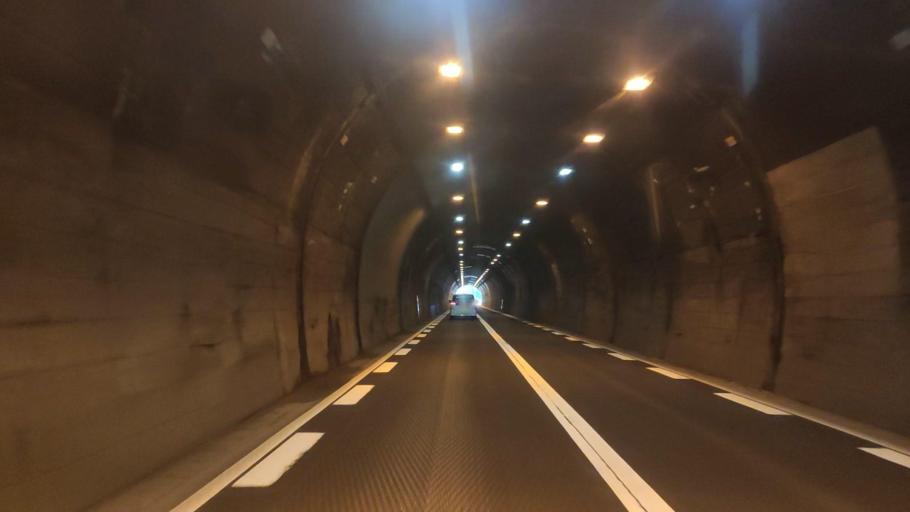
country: JP
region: Fukui
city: Takefu
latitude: 35.7867
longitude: 136.0993
